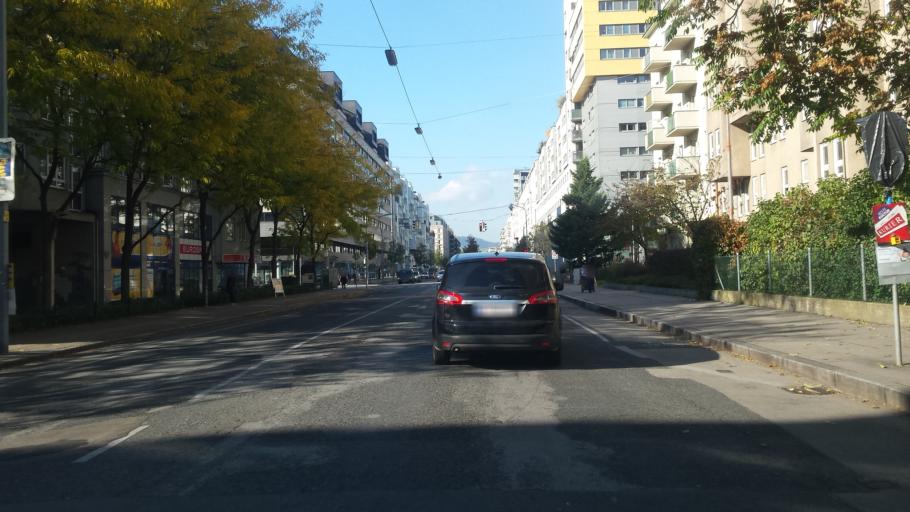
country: AT
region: Vienna
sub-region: Wien Stadt
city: Vienna
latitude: 48.2247
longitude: 16.4013
